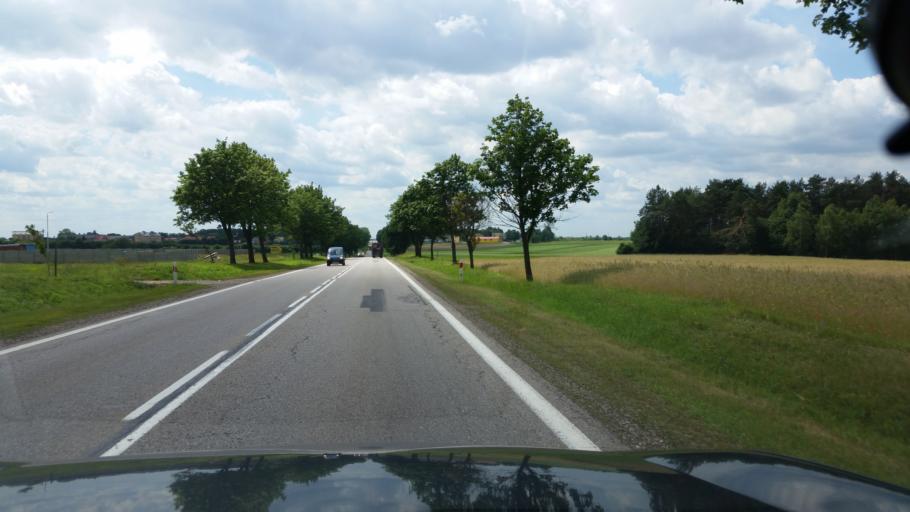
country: PL
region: Podlasie
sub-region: Powiat lomzynski
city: Piatnica
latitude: 53.2192
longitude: 22.1074
